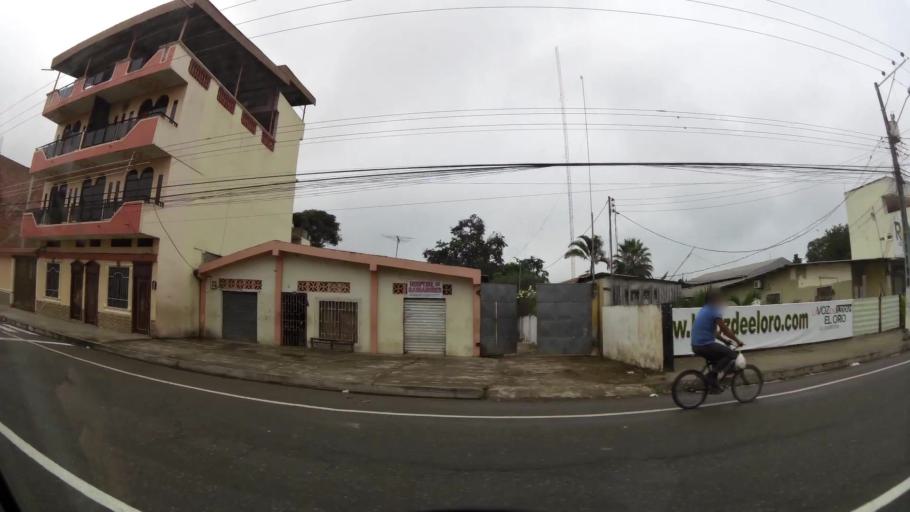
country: EC
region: El Oro
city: Pasaje
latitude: -3.3290
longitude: -79.8165
